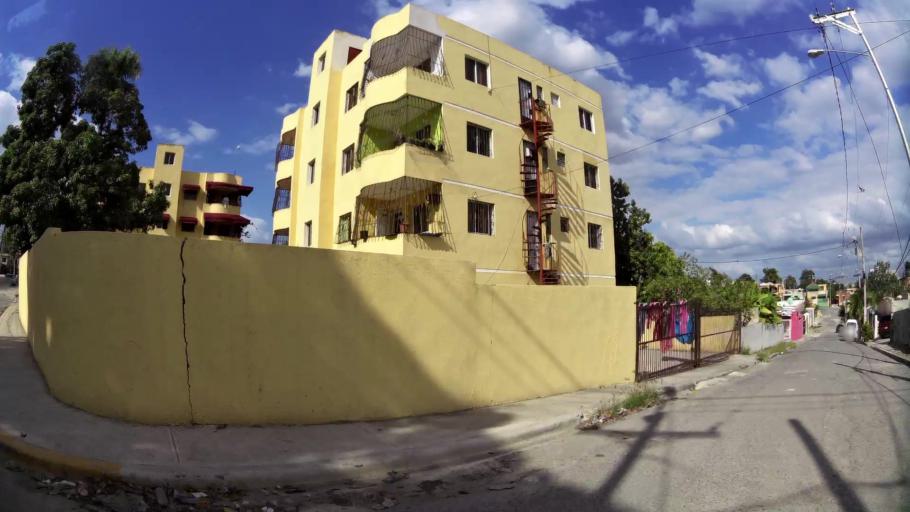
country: DO
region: Nacional
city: Ensanche Luperon
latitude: 18.5390
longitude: -69.8969
